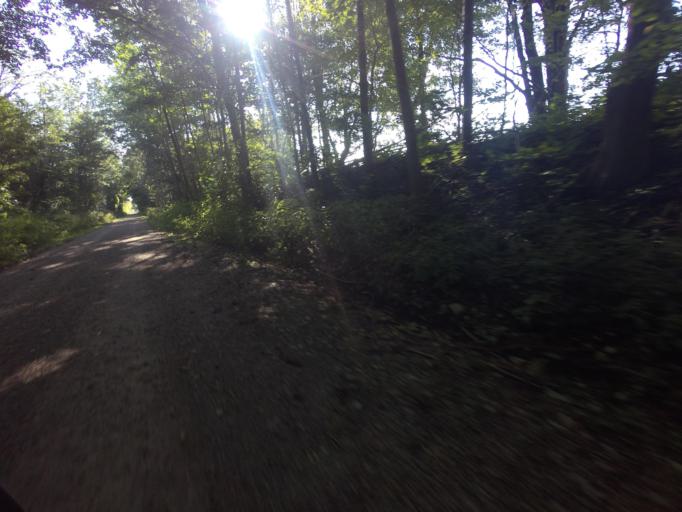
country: CA
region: Ontario
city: Huron East
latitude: 43.7384
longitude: -81.4444
